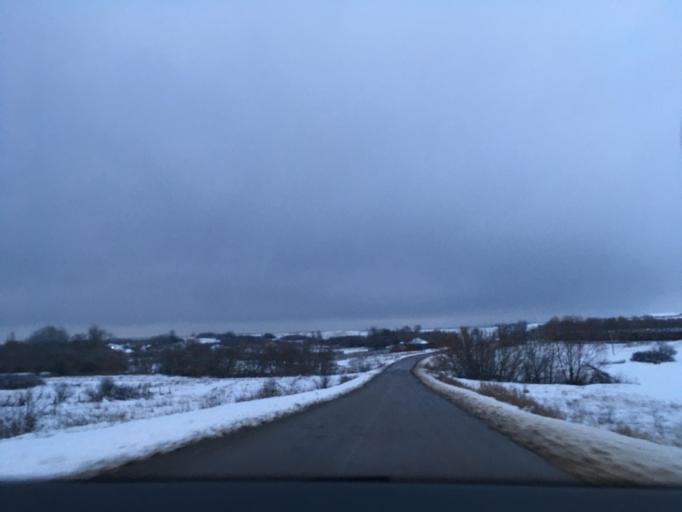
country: RU
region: Voronezj
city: Verkhniy Mamon
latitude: 50.0714
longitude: 40.3160
